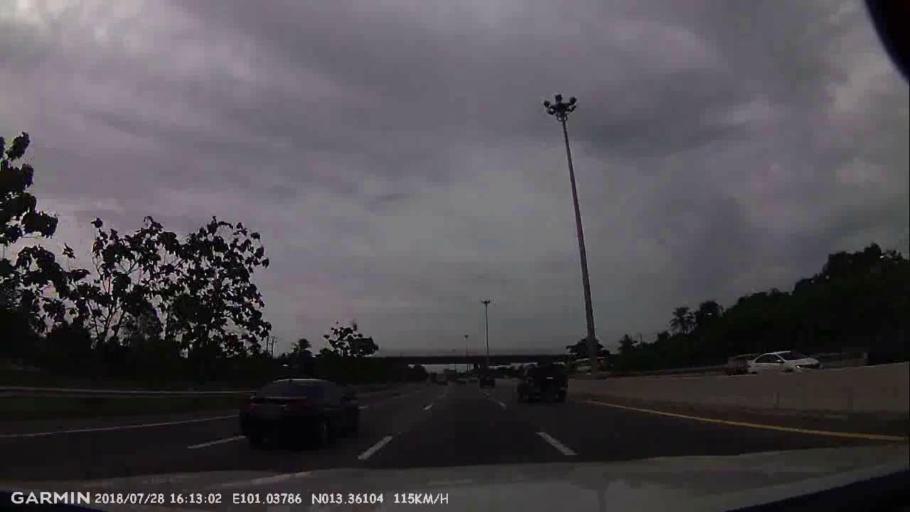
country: TH
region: Chon Buri
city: Chon Buri
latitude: 13.3614
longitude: 101.0380
